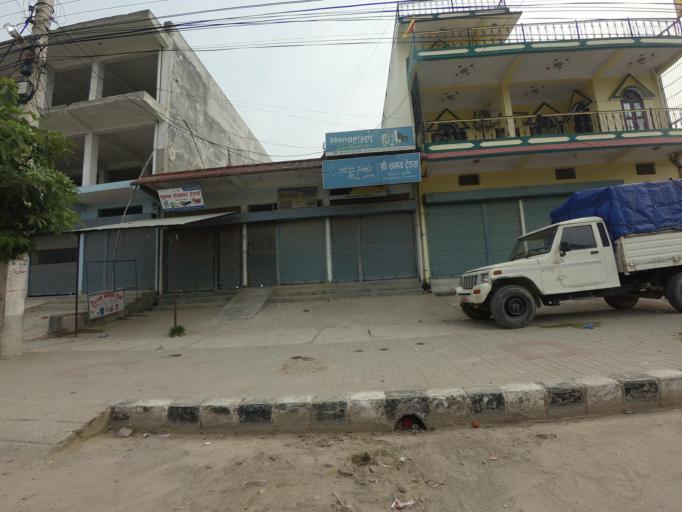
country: NP
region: Western Region
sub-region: Lumbini Zone
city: Bhairahawa
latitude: 27.5079
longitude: 83.4396
